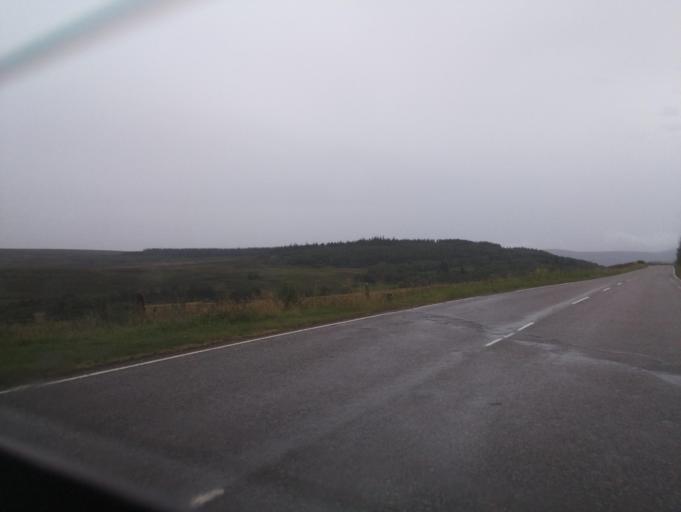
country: GB
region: Scotland
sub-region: Highland
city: Grantown on Spey
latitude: 57.2463
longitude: -3.3609
